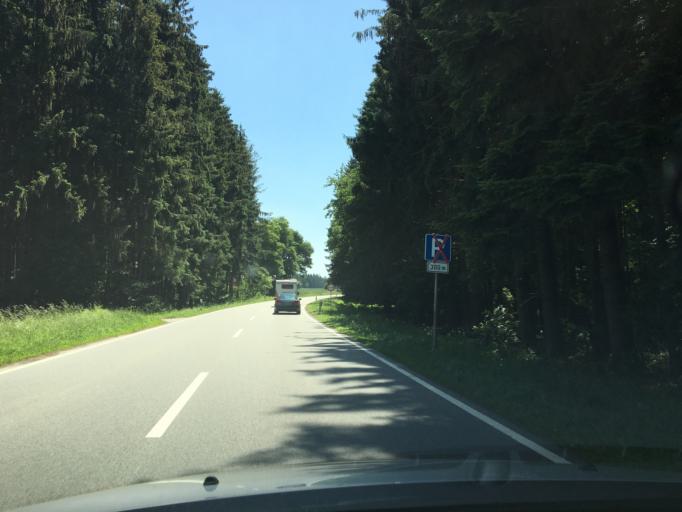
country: DE
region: Bavaria
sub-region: Upper Bavaria
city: Niedertaufkirchen
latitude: 48.3350
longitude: 12.5225
